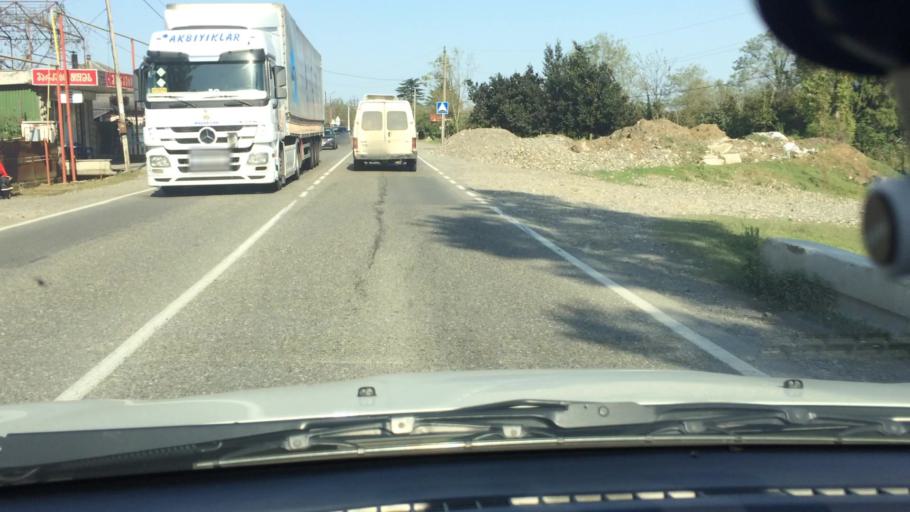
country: GE
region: Guria
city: Lanchkhuti
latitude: 42.0769
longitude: 42.0523
